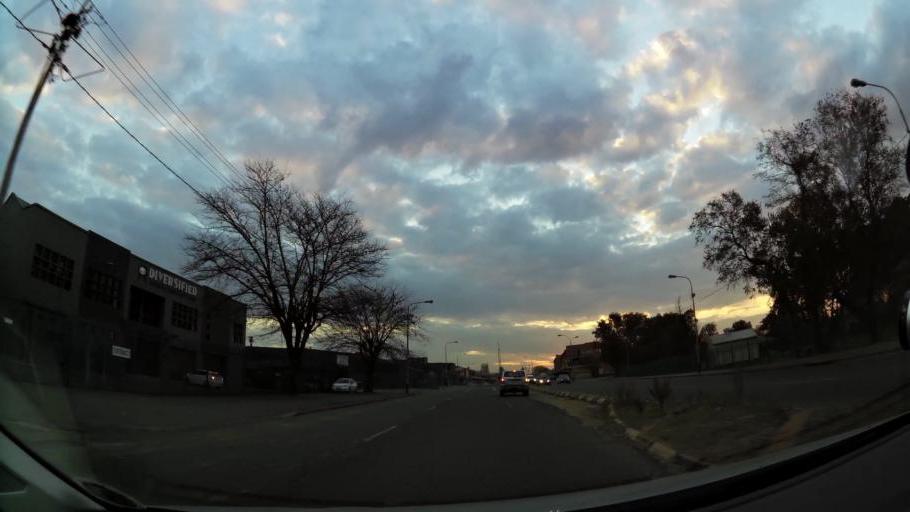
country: ZA
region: Gauteng
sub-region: Ekurhuleni Metropolitan Municipality
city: Germiston
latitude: -26.2036
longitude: 28.1272
